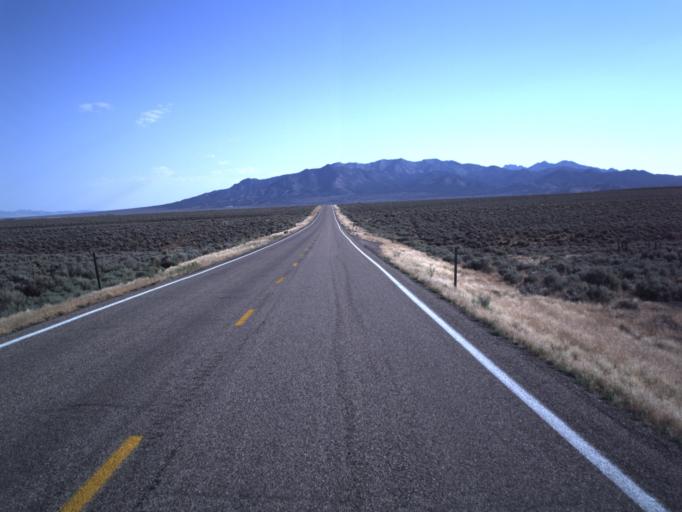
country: US
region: Utah
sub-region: Beaver County
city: Milford
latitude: 38.1552
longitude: -112.9582
